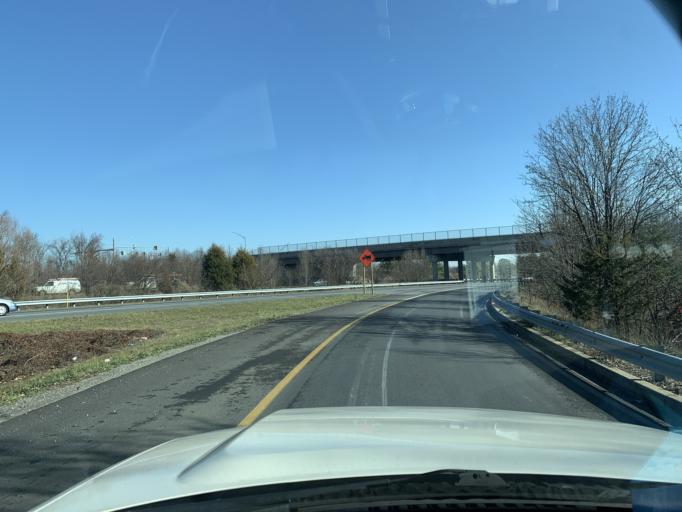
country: US
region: Maryland
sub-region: Howard County
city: Fort George G Mead Junction
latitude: 39.1284
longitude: -76.7964
